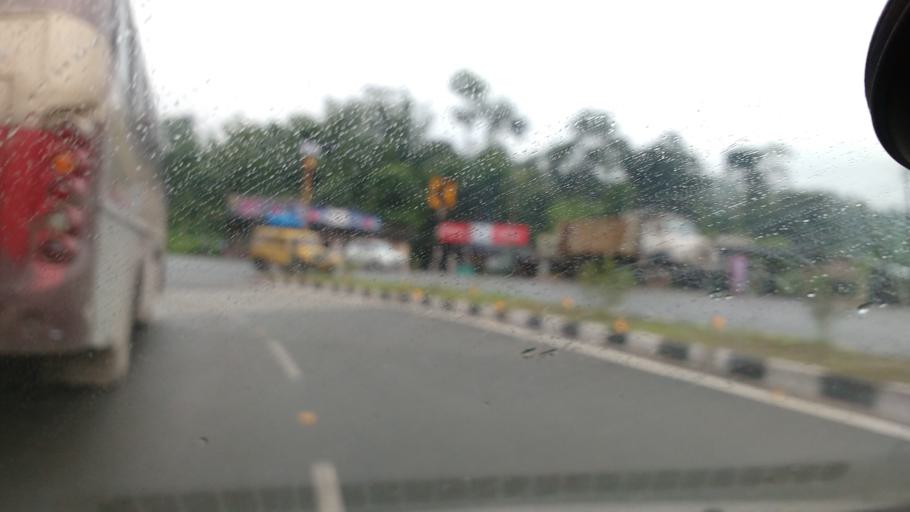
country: IN
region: Meghalaya
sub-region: Ri-Bhoi
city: Nongpoh
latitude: 25.8323
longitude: 91.8769
